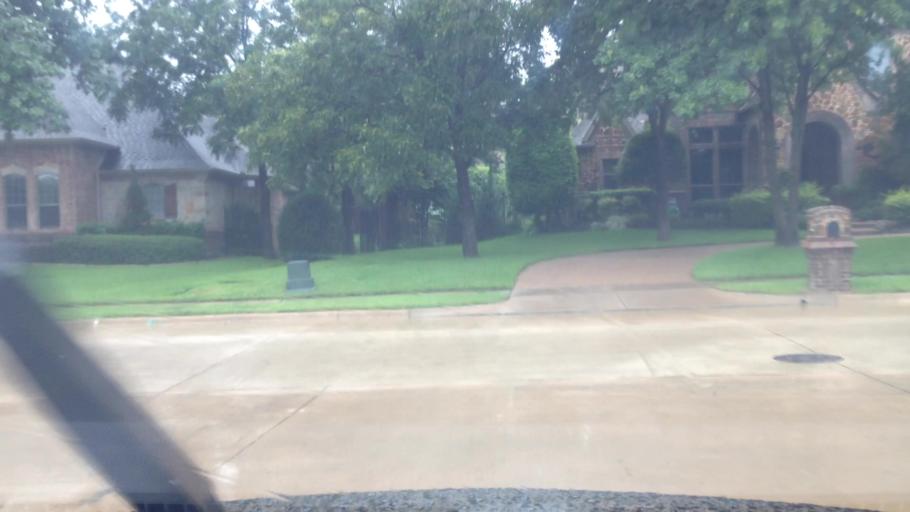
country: US
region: Texas
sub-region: Tarrant County
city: Keller
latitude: 32.9126
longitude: -97.2260
